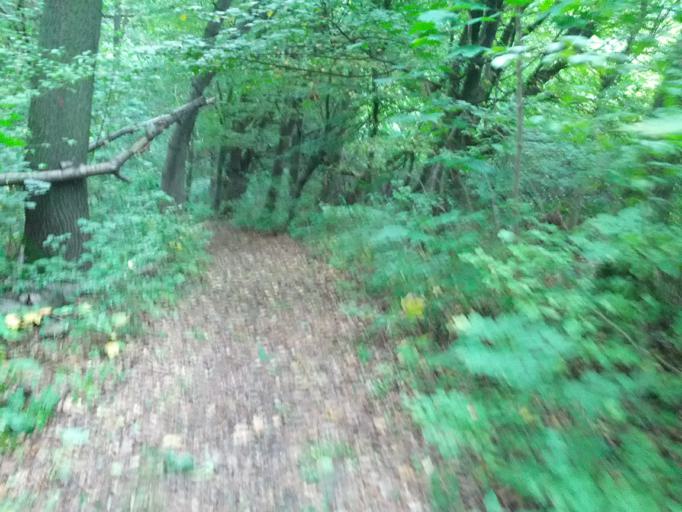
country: DE
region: Thuringia
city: Krauthausen
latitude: 50.9918
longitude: 10.2779
